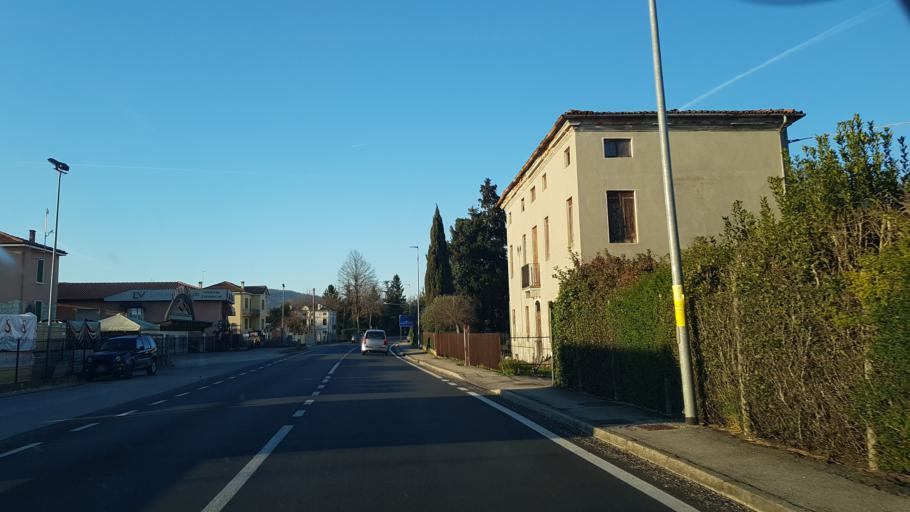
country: IT
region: Veneto
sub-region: Provincia di Vicenza
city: Ponte di Castegnero
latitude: 45.4342
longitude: 11.5987
